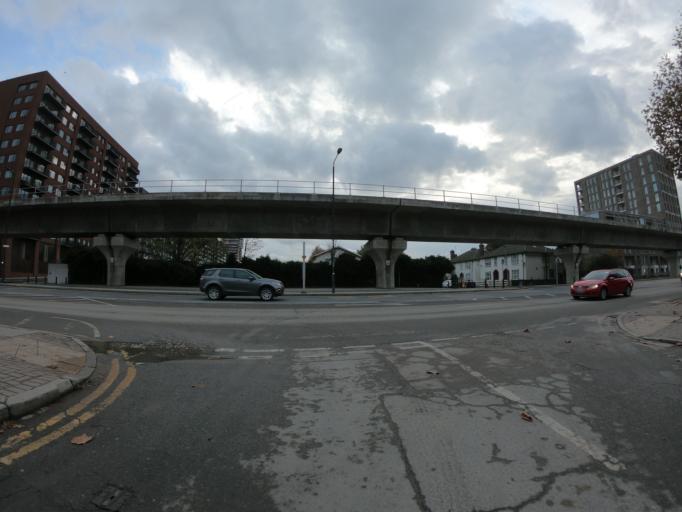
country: GB
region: England
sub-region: Greater London
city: East Ham
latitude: 51.5026
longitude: 0.0255
